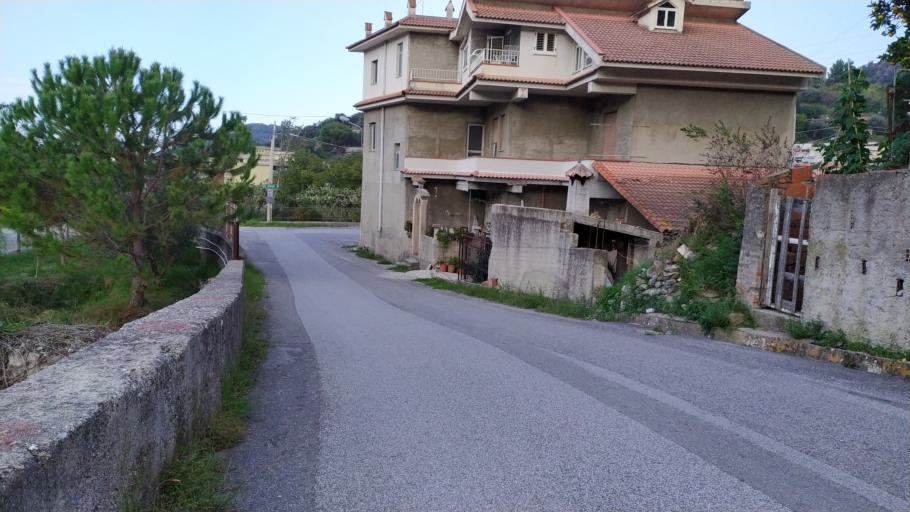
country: IT
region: Sicily
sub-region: Messina
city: Saponara
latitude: 38.1944
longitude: 15.4300
